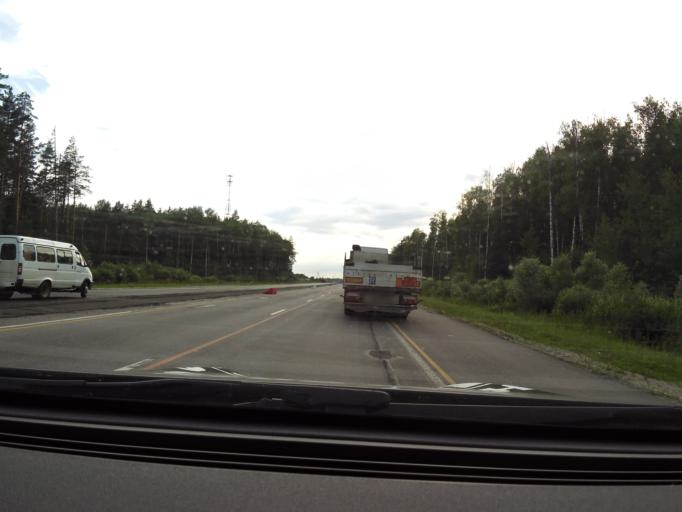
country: RU
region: Vladimir
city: Orgtrud
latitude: 56.1033
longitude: 40.6984
